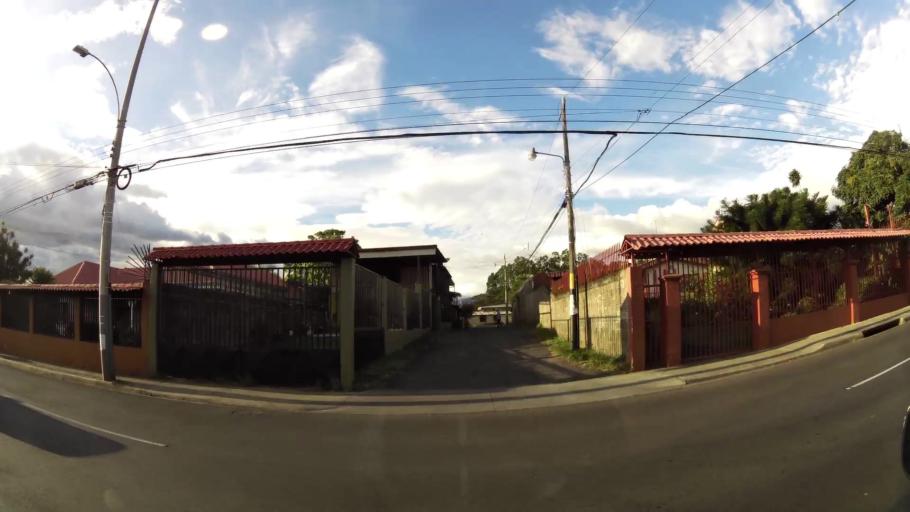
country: CR
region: Heredia
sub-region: Canton de Belen
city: San Antonio
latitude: 10.0054
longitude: -84.1807
